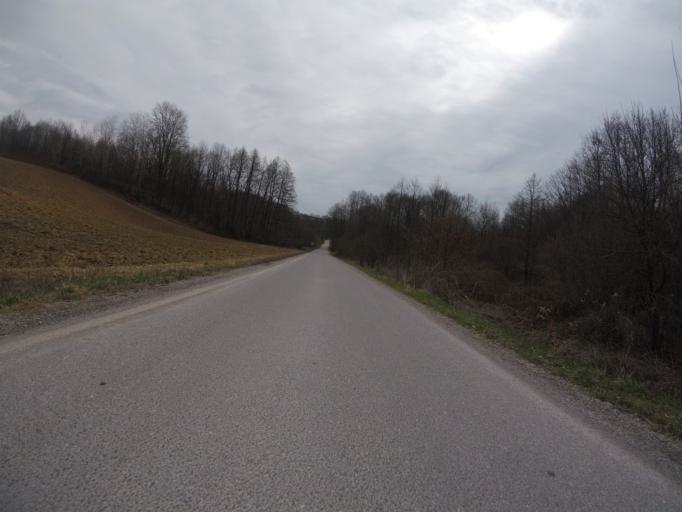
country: HR
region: Grad Zagreb
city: Strmec
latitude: 45.5957
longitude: 15.9141
